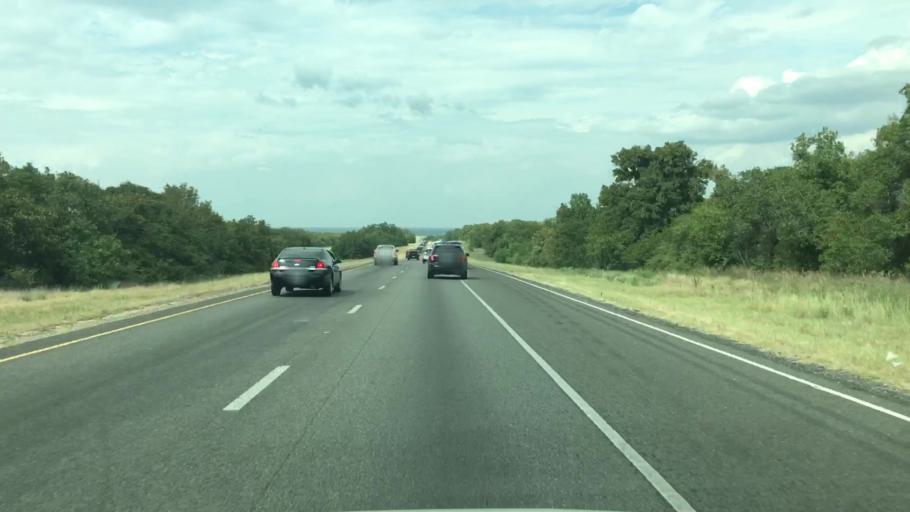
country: US
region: Texas
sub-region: Bexar County
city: Elmendorf
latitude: 29.1899
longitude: -98.4233
